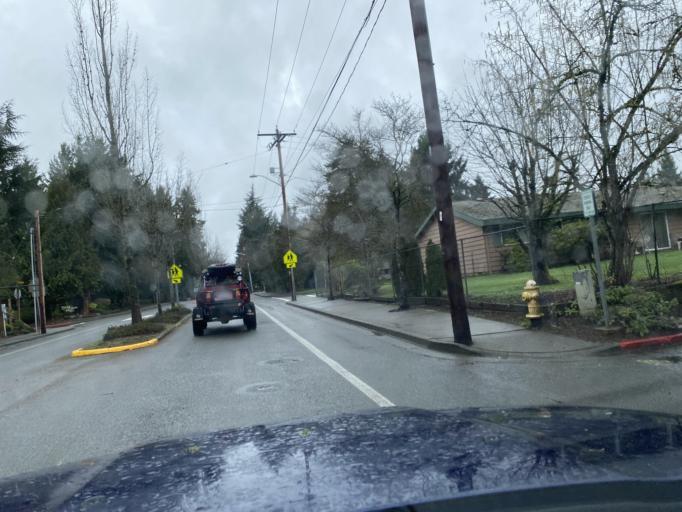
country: US
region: Washington
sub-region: King County
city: Eastgate
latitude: 47.6099
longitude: -122.1455
